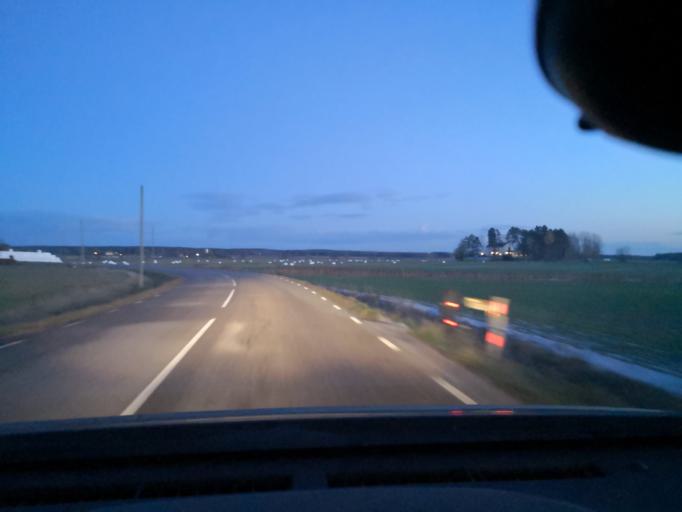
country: SE
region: Vaestmanland
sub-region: Sala Kommun
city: Sala
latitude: 59.8713
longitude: 16.7092
